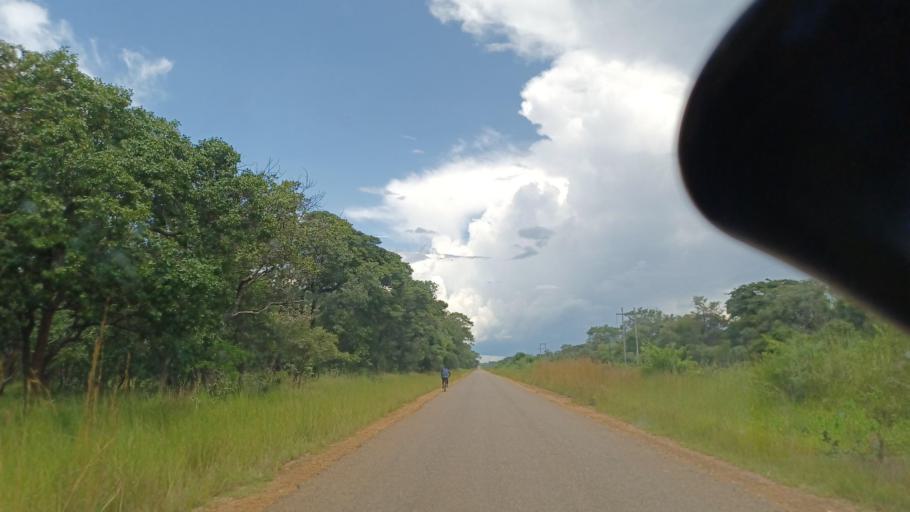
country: ZM
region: North-Western
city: Kasempa
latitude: -12.8797
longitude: 26.0451
